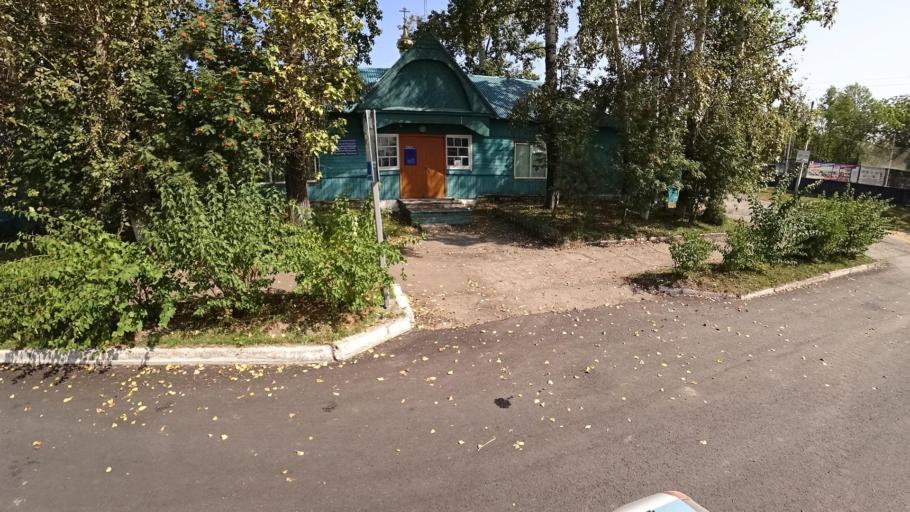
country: RU
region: Khabarovsk Krai
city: Khor
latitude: 47.9644
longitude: 135.0533
